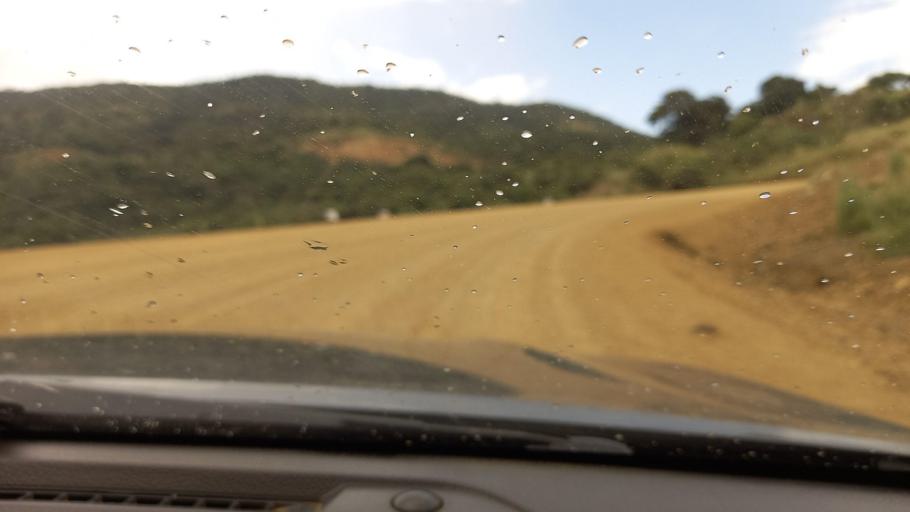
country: ET
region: Southern Nations, Nationalities, and People's Region
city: Mizan Teferi
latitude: 6.2037
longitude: 35.6706
